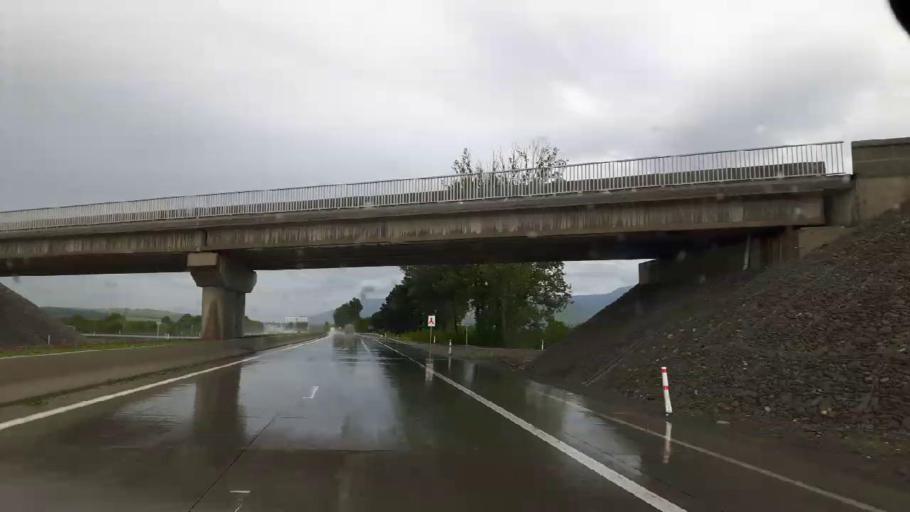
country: GE
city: Agara
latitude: 42.0315
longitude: 43.9499
